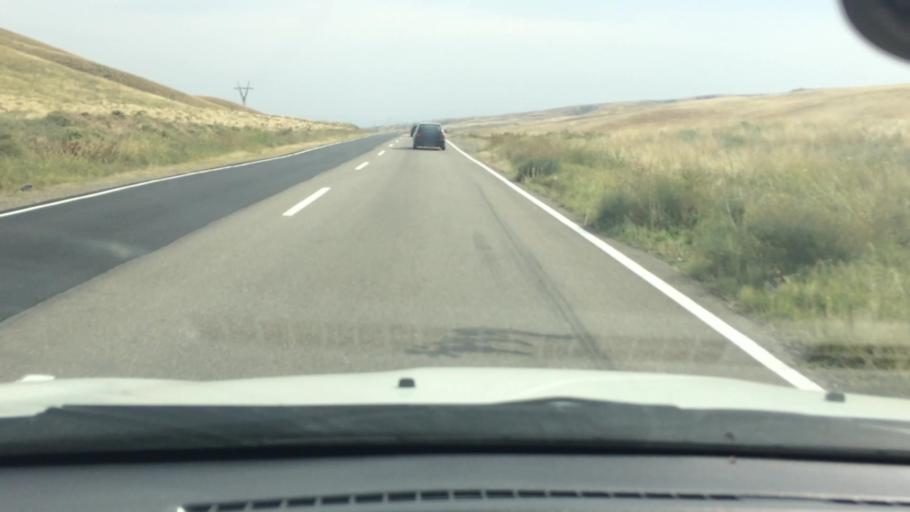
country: GE
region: Kvemo Kartli
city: Rust'avi
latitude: 41.5125
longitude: 44.9471
